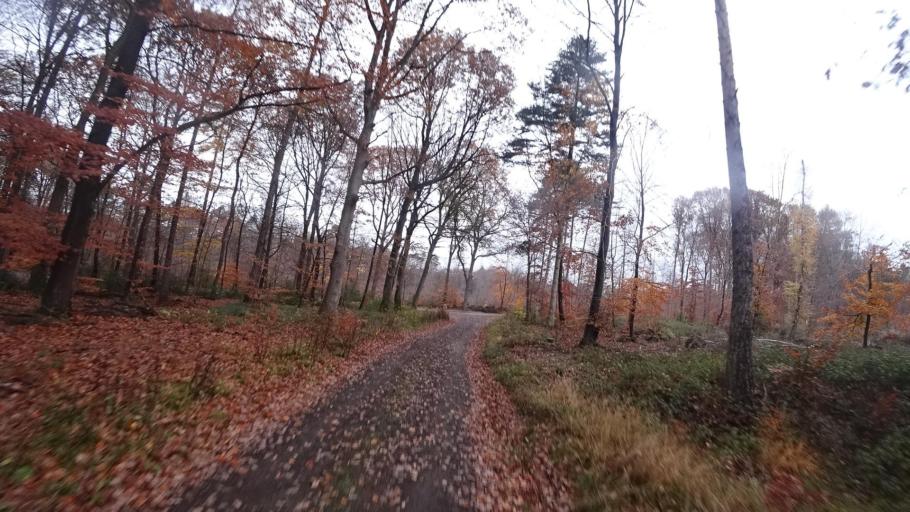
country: DE
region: Rheinland-Pfalz
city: Bad Neuenahr-Ahrweiler
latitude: 50.5313
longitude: 7.1257
